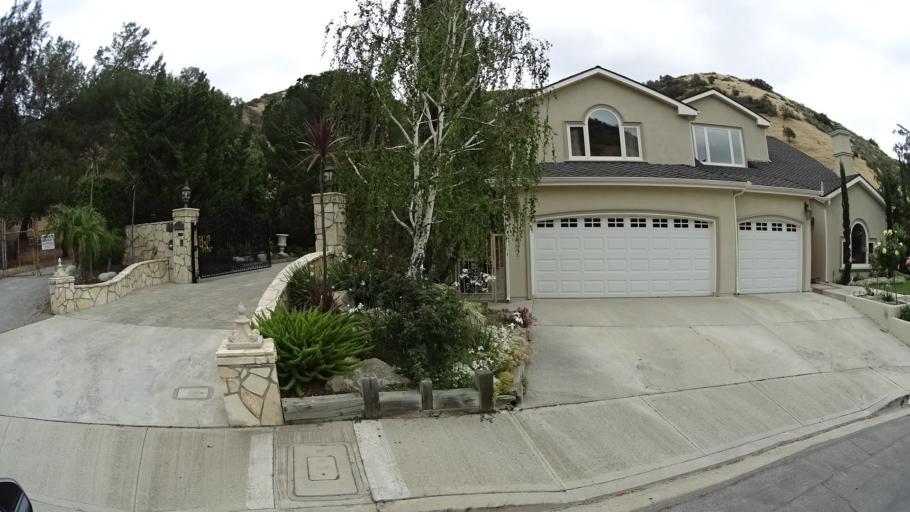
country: US
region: California
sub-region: Los Angeles County
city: Burbank
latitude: 34.2141
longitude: -118.3231
